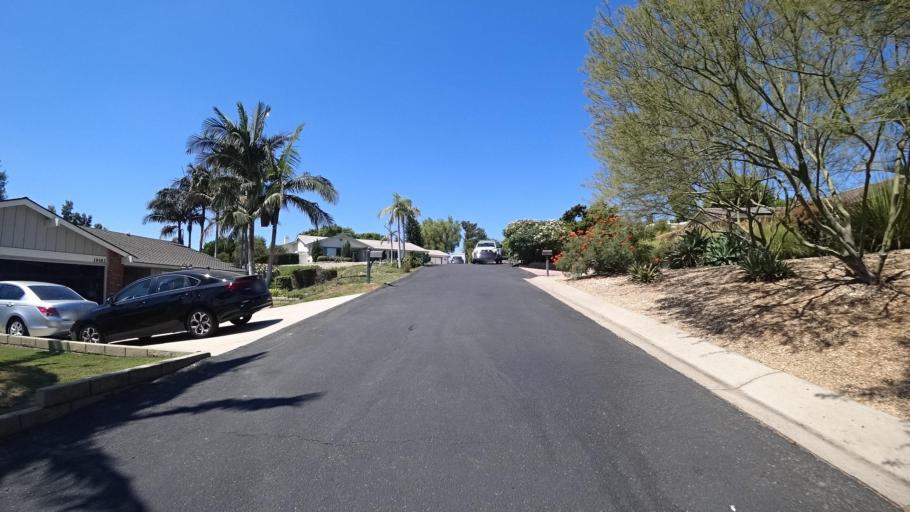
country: US
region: California
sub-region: Orange County
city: Yorba Linda
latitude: 33.8814
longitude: -117.8000
